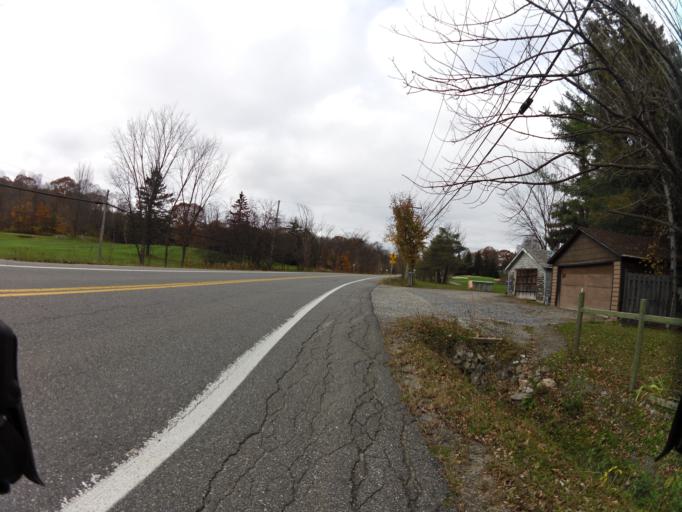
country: CA
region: Quebec
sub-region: Outaouais
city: Wakefield
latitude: 45.5521
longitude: -75.8266
